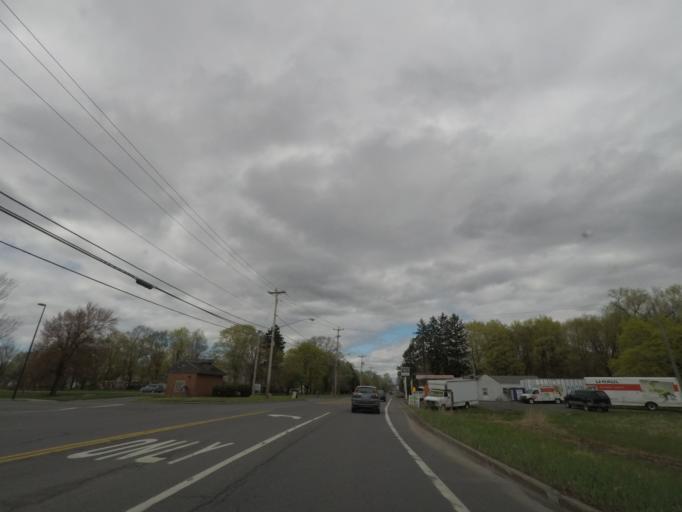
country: US
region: New York
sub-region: Columbia County
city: Chatham
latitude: 42.3502
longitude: -73.6037
